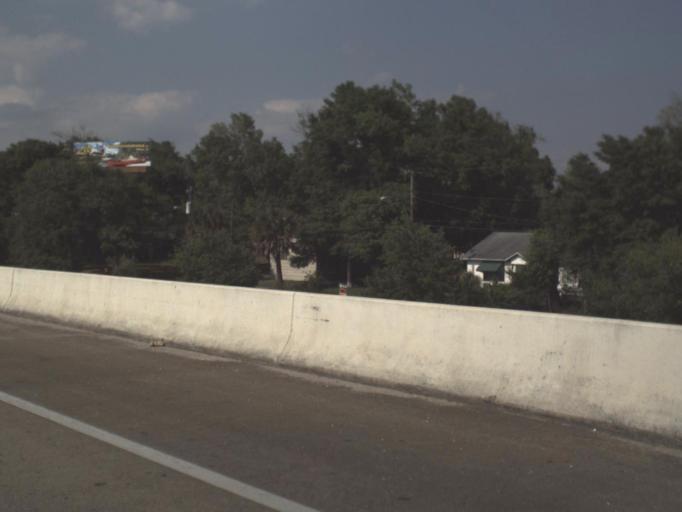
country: US
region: Florida
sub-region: Escambia County
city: Pensacola
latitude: 30.4287
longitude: -87.2151
